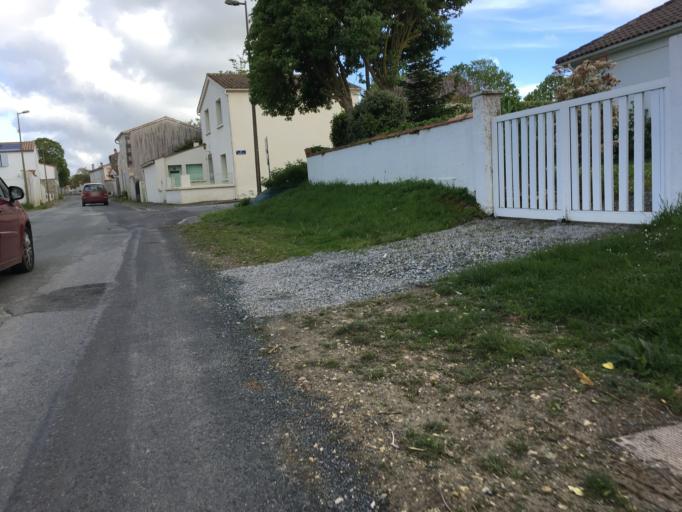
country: FR
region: Poitou-Charentes
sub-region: Departement de la Charente-Maritime
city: Bourgneuf
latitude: 46.1707
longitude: -1.0238
